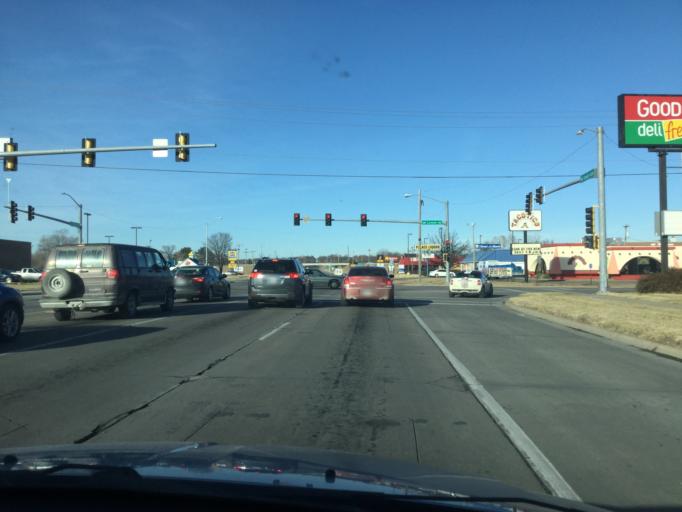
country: US
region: Kansas
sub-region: Shawnee County
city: Topeka
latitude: 39.0872
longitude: -95.6646
